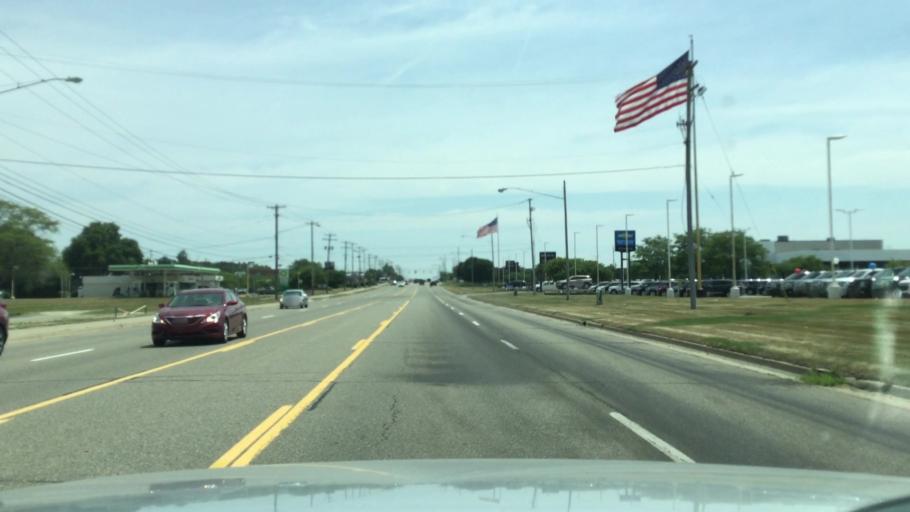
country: US
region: Michigan
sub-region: Genesee County
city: Swartz Creek
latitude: 43.0019
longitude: -83.7790
